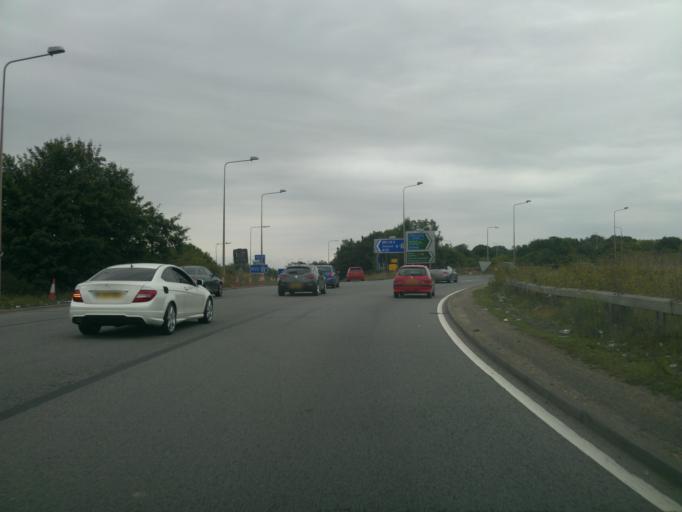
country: GB
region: England
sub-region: Essex
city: Aveley
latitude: 51.4982
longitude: 0.2667
